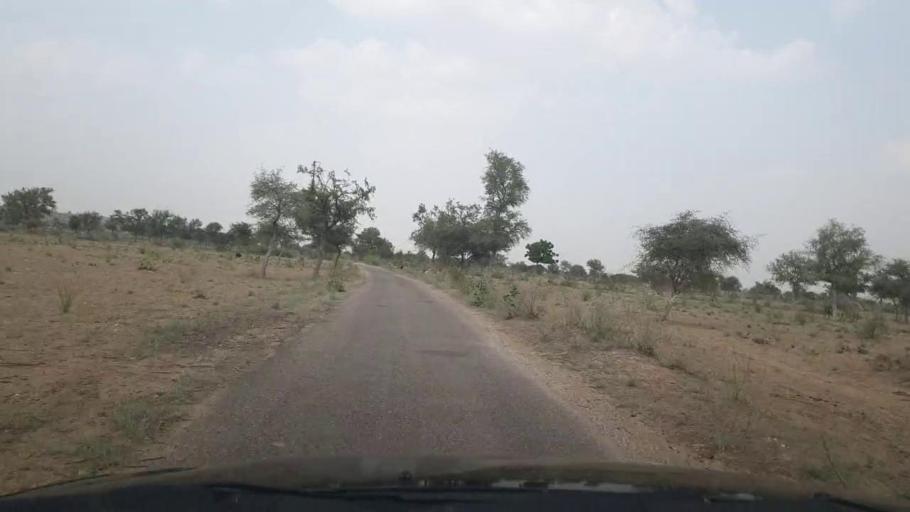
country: PK
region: Sindh
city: Islamkot
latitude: 24.9271
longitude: 70.5643
